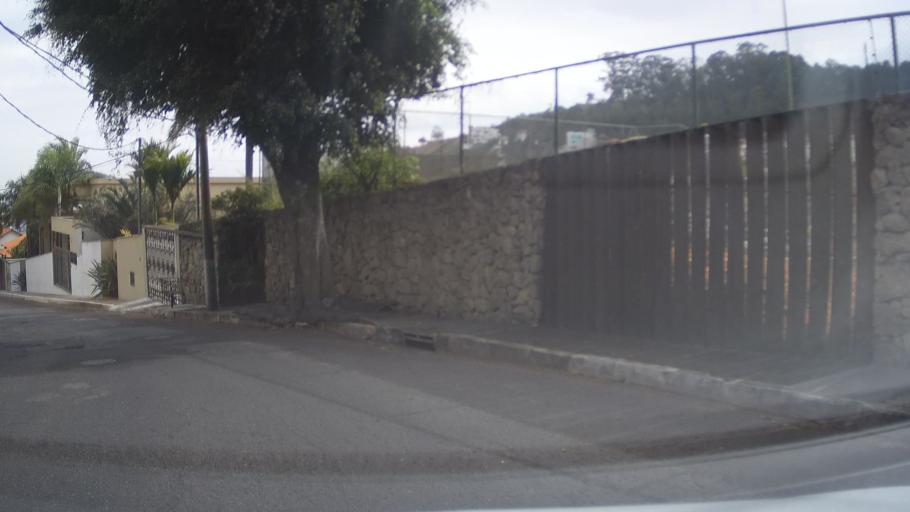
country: BR
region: Minas Gerais
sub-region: Belo Horizonte
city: Belo Horizonte
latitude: -19.9549
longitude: -43.9166
